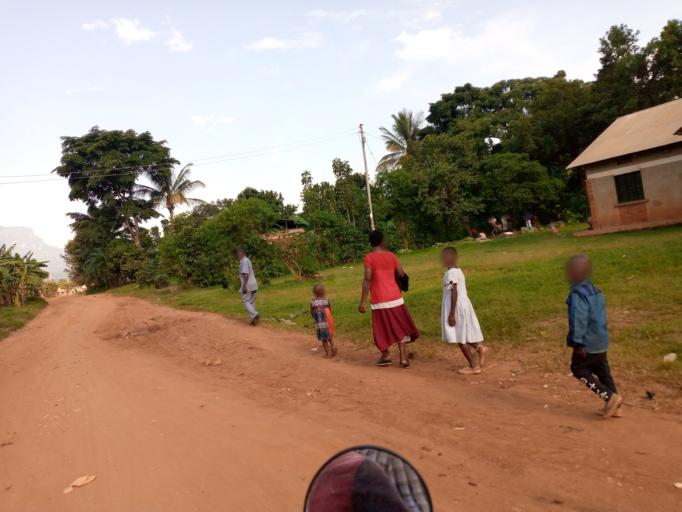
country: UG
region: Eastern Region
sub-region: Mbale District
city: Mbale
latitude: 1.0540
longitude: 34.1656
